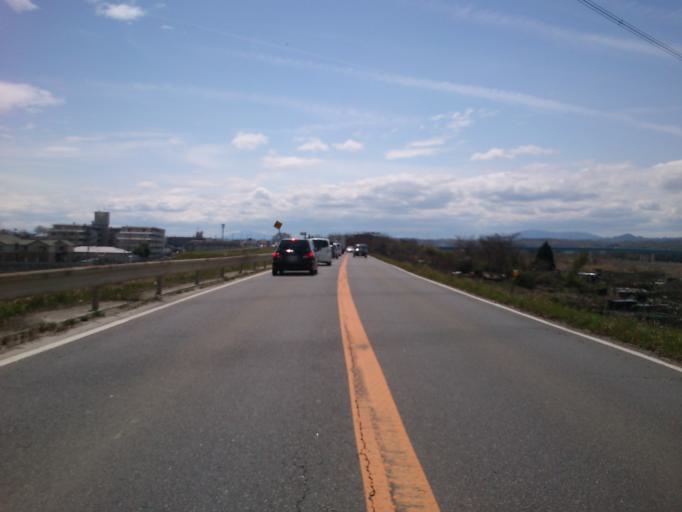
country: JP
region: Kyoto
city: Tanabe
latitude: 34.8042
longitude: 135.8045
